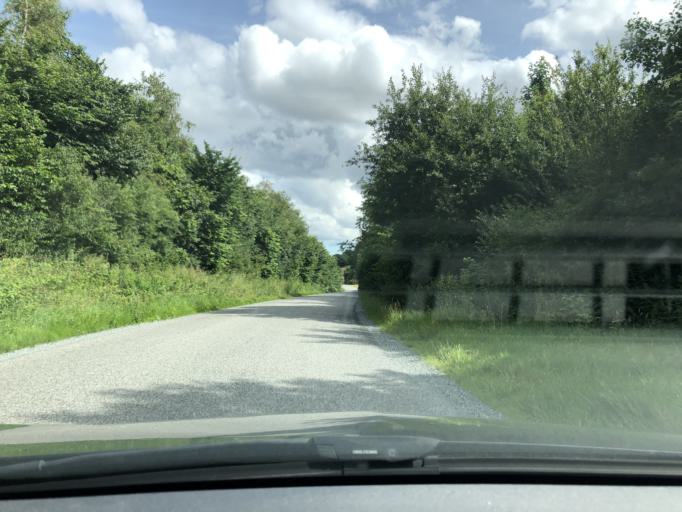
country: DK
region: South Denmark
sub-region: Vejle Kommune
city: Jelling
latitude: 55.6971
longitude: 9.4503
